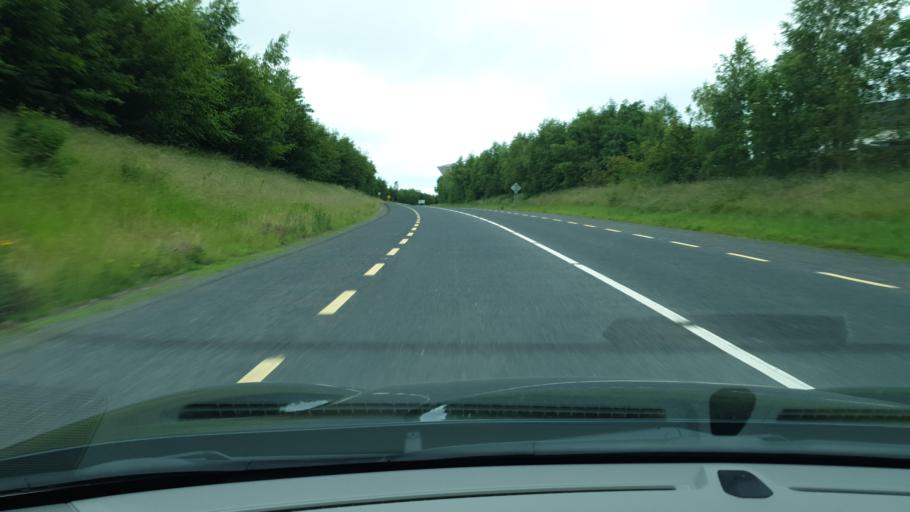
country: IE
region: Leinster
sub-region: An Mhi
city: Dunshaughlin
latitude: 53.5178
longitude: -6.5542
